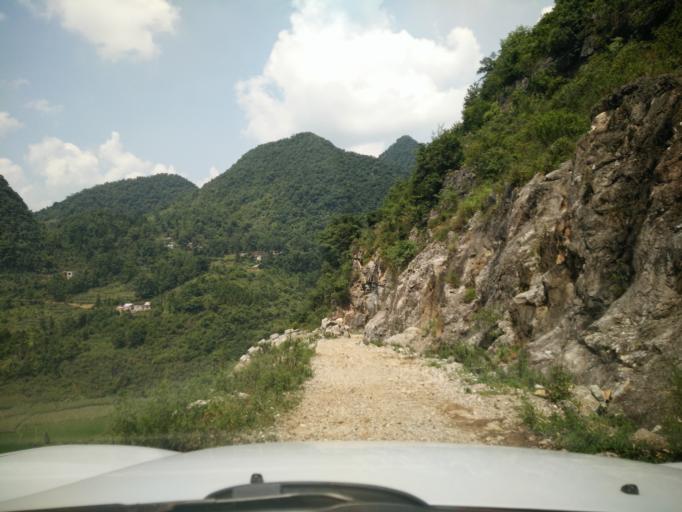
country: CN
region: Guangxi Zhuangzu Zizhiqu
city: Xinzhou
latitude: 25.0227
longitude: 105.7051
